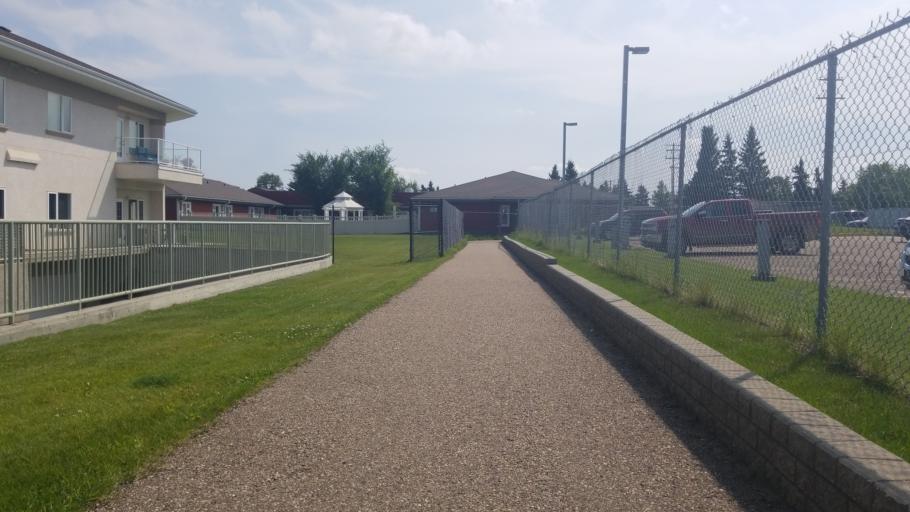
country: CA
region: Saskatchewan
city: Lloydminster
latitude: 53.2747
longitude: -110.0173
